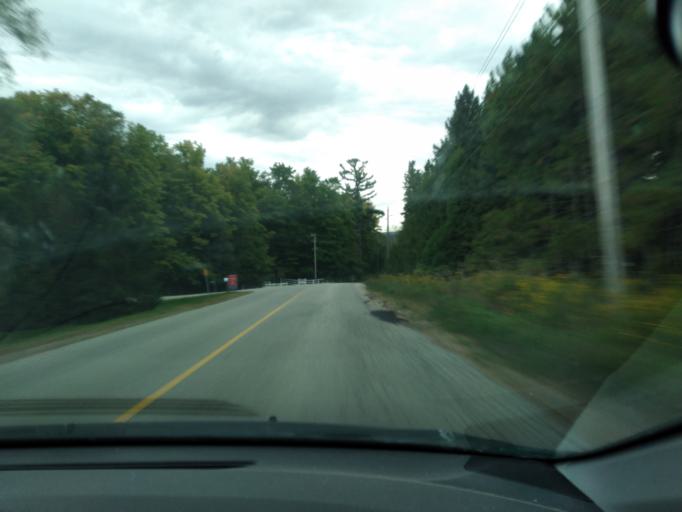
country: CA
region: Ontario
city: Bradford West Gwillimbury
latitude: 43.9513
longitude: -79.7786
